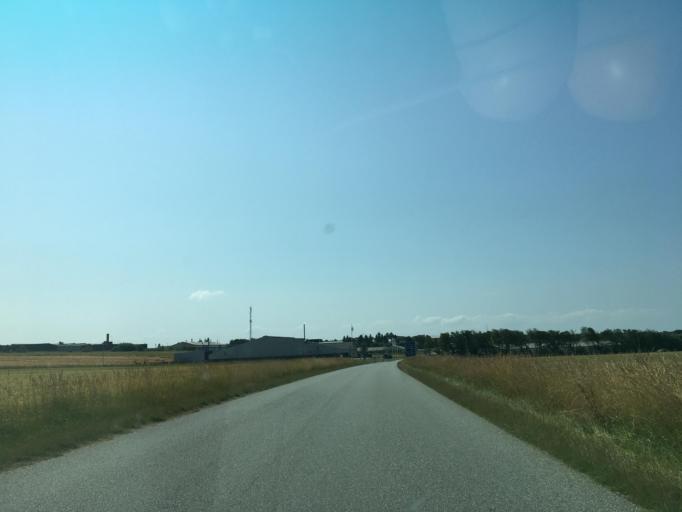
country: DK
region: North Denmark
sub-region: Thisted Kommune
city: Hurup
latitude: 56.7546
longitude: 8.4371
